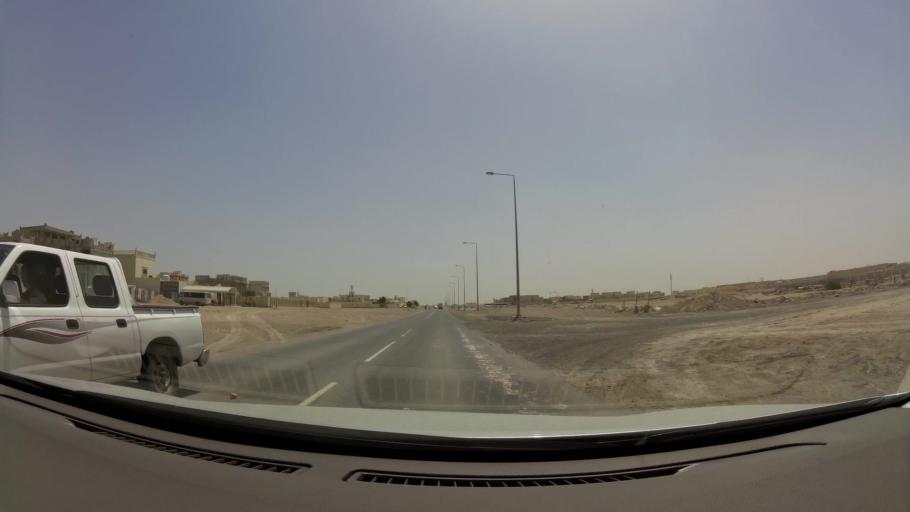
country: QA
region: Baladiyat Umm Salal
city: Umm Salal Muhammad
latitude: 25.3923
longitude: 51.4465
